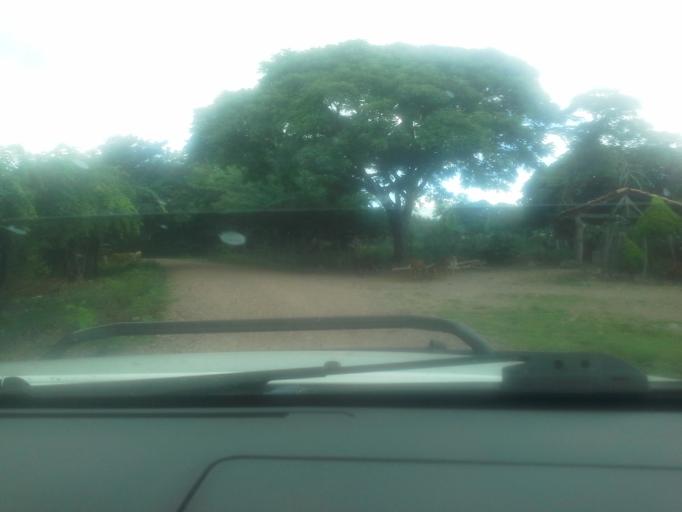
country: NI
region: Matagalpa
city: Ciudad Dario
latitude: 12.8232
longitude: -86.1913
